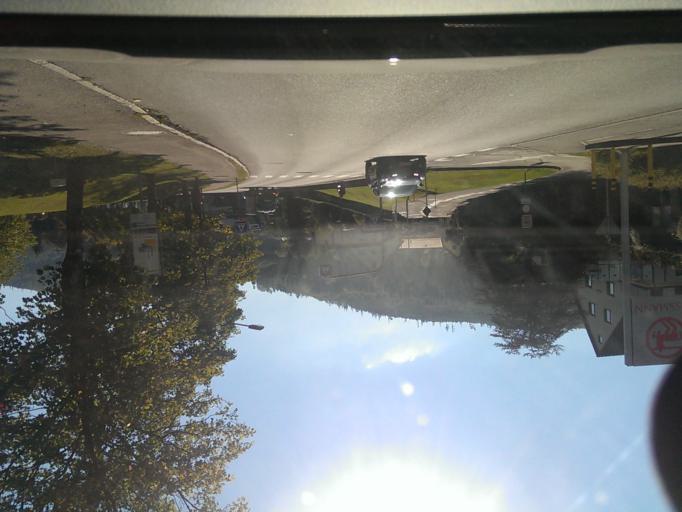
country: DE
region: Baden-Wuerttemberg
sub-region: Karlsruhe Region
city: Bad Herrenalb
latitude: 48.8065
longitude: 8.4450
